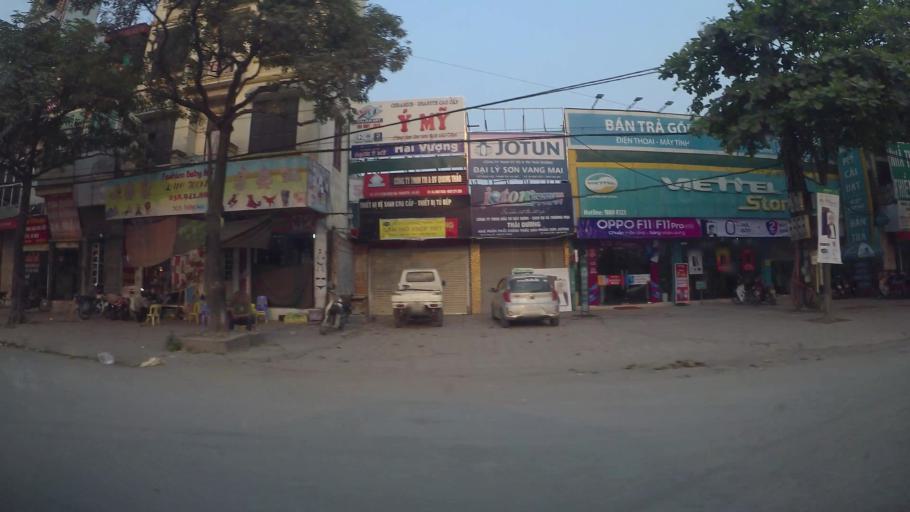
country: VN
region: Ha Noi
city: Van Dien
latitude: 20.9433
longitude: 105.8443
